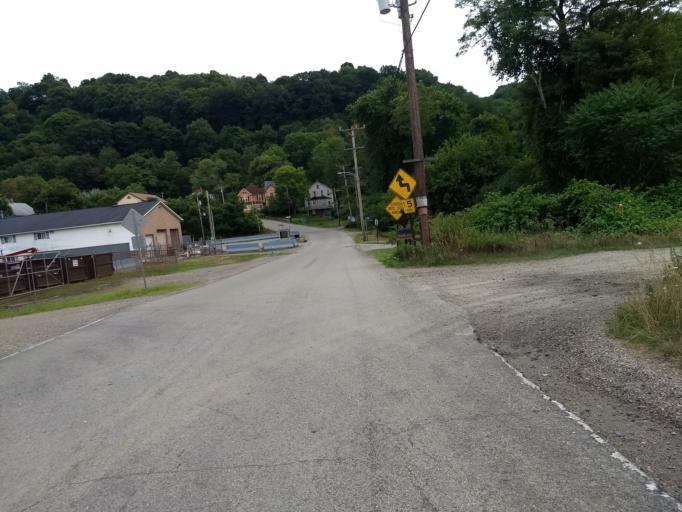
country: US
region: Pennsylvania
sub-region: Allegheny County
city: Brackenridge
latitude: 40.6126
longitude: -79.7143
